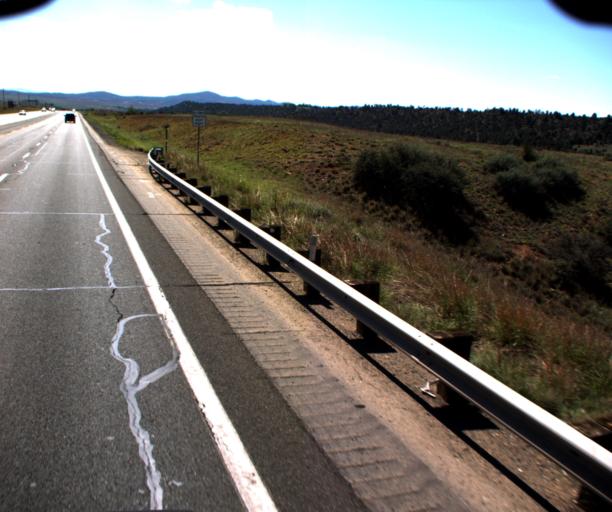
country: US
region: Arizona
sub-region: Yavapai County
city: Prescott Valley
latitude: 34.5780
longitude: -112.2936
